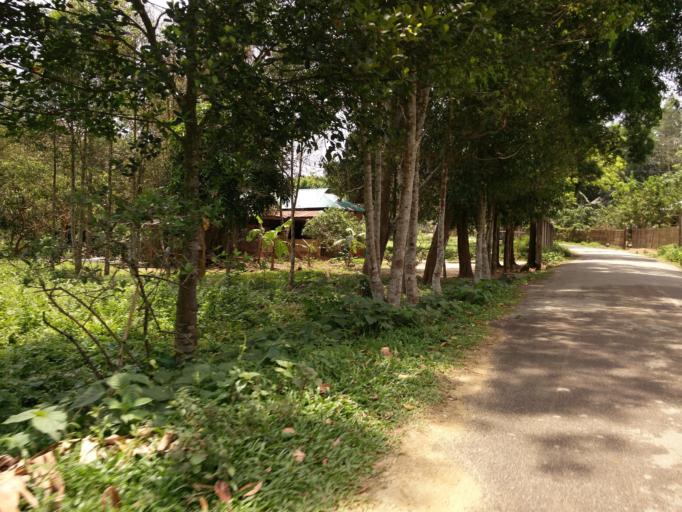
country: IN
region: Tripura
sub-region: Dhalai
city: Kamalpur
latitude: 24.3033
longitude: 91.7784
